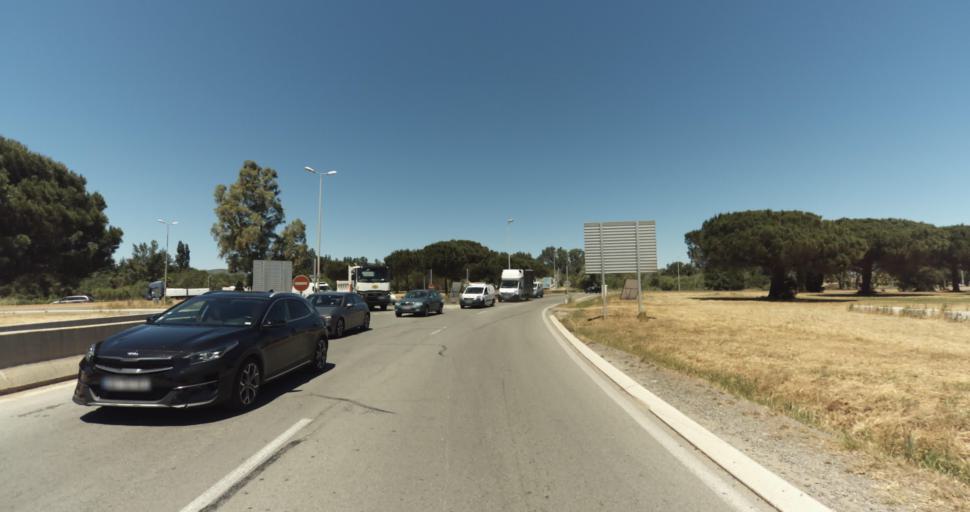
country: FR
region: Provence-Alpes-Cote d'Azur
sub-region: Departement du Var
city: Gassin
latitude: 43.2619
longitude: 6.5748
